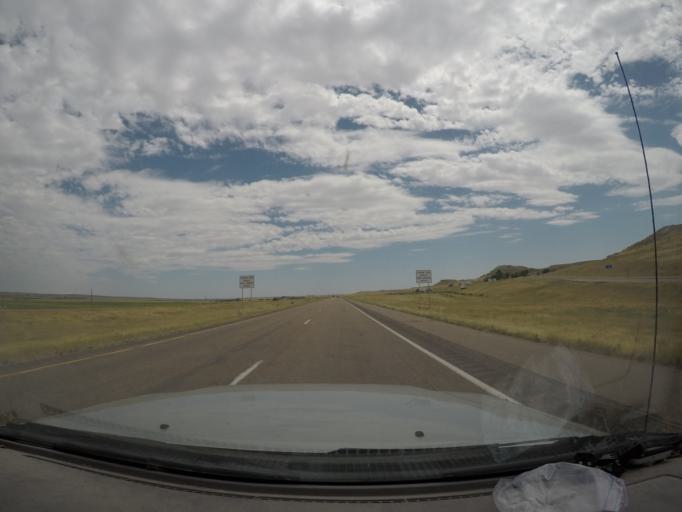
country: US
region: Nebraska
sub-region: Cheyenne County
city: Sidney
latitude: 41.1580
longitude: -103.0920
